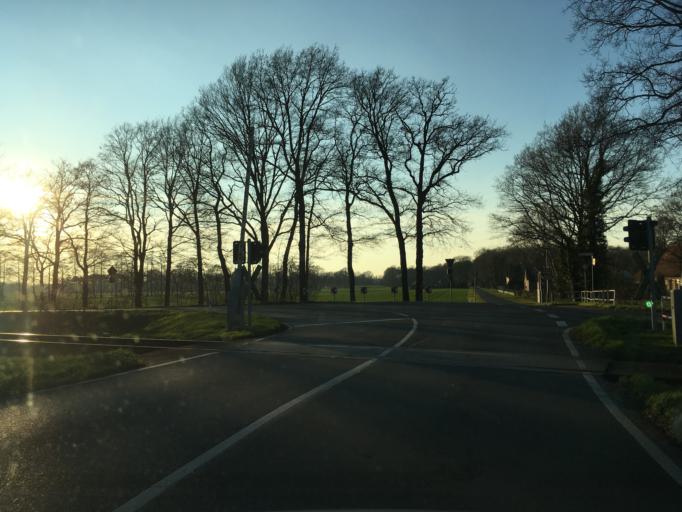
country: DE
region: North Rhine-Westphalia
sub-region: Regierungsbezirk Munster
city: Gronau
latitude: 52.1629
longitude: 7.0280
